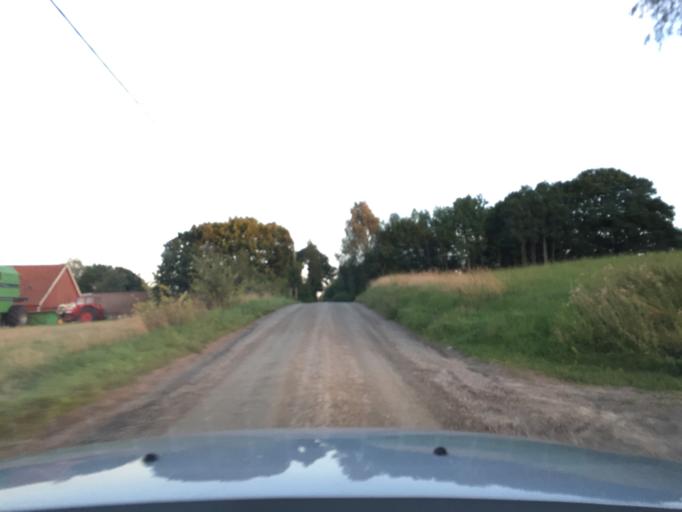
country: SE
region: Skane
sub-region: Hassleholms Kommun
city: Sosdala
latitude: 56.0061
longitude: 13.6592
